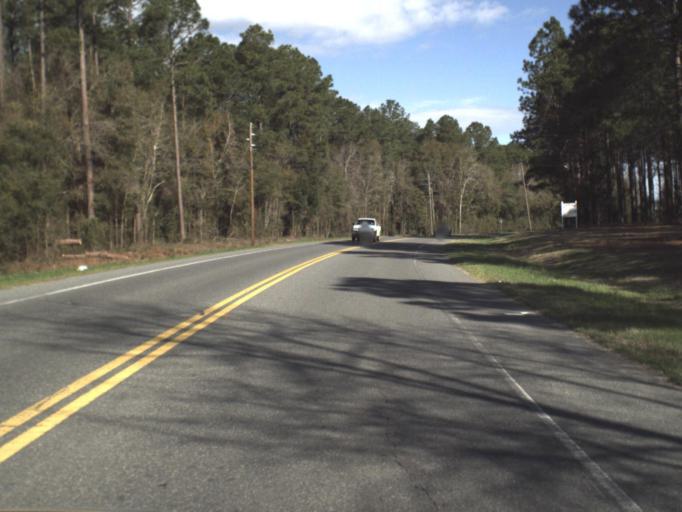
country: US
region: Florida
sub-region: Jackson County
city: Malone
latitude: 30.9317
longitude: -85.1657
